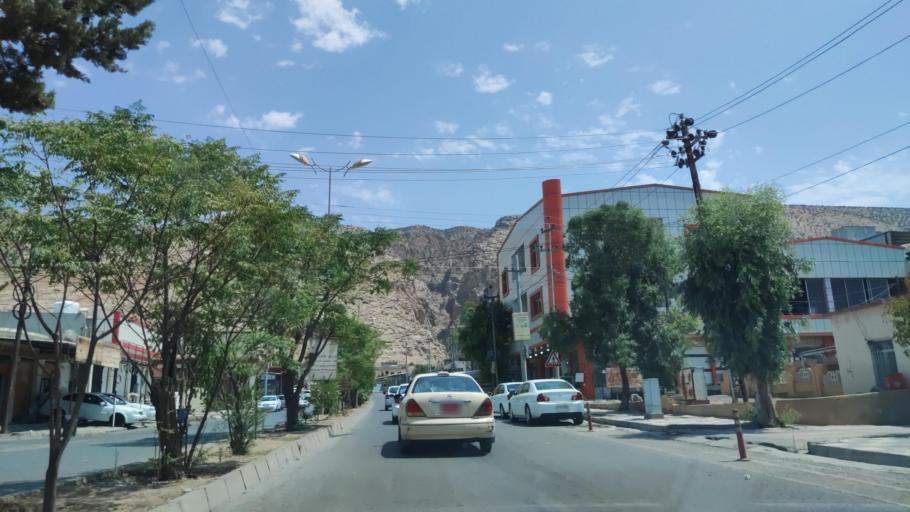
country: IQ
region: Arbil
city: Shaqlawah
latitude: 36.5494
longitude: 44.3527
